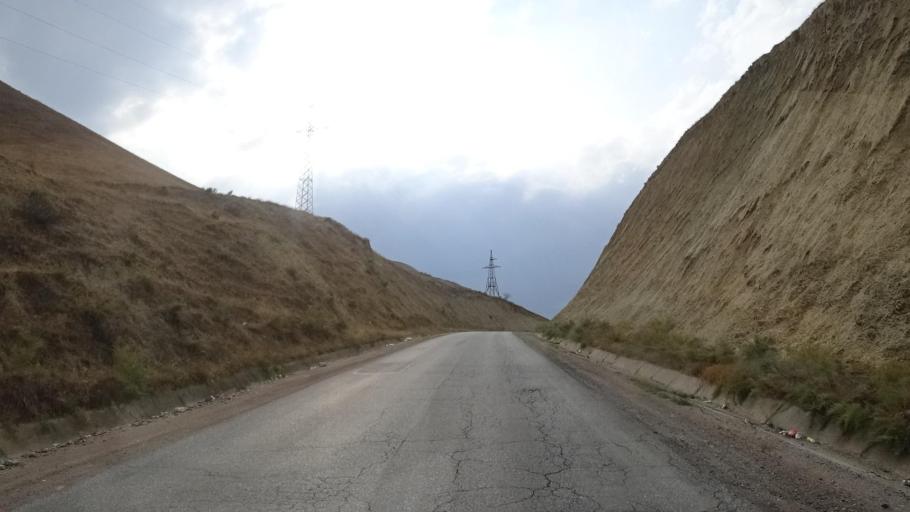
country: KG
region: Jalal-Abad
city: Uch-Terek
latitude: 41.8195
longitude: 73.1855
